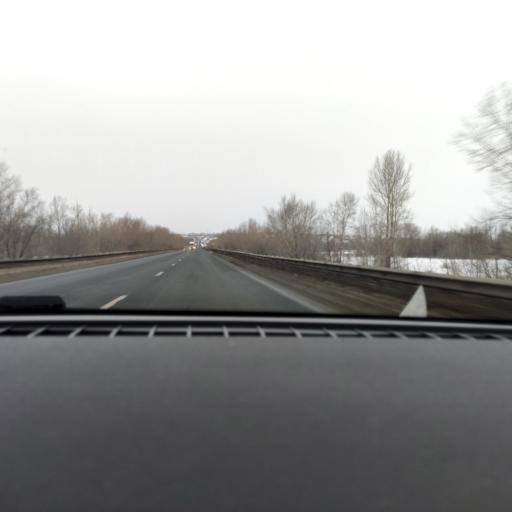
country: RU
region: Samara
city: Smyshlyayevka
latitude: 53.2202
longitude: 50.5002
